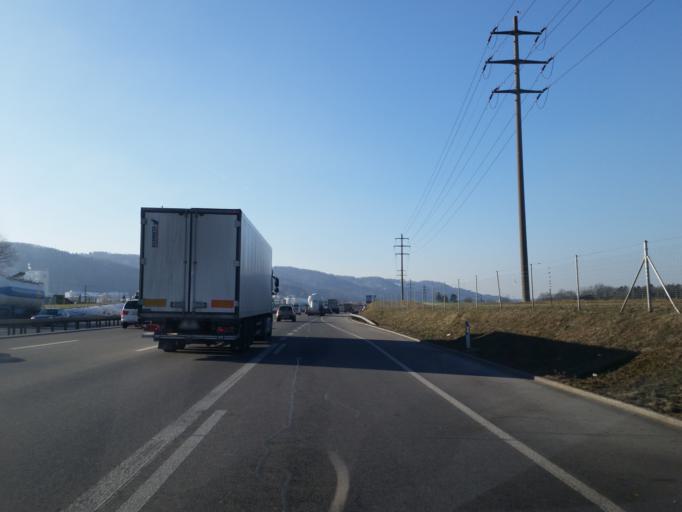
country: CH
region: Zurich
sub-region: Bezirk Dietikon
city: Dietikon / Vorstadt
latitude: 47.4232
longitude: 8.3867
